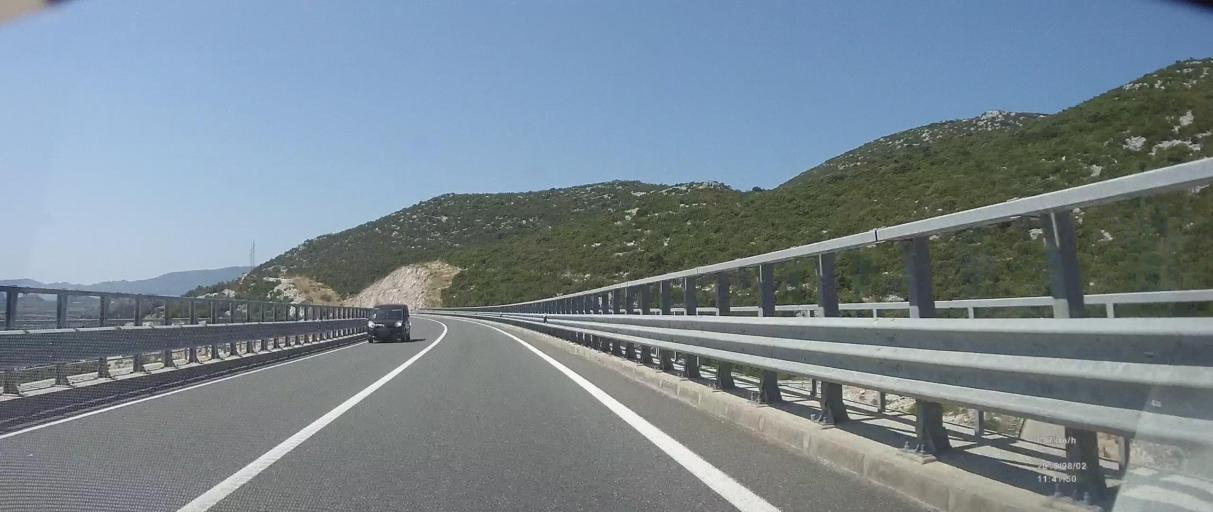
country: HR
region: Dubrovacko-Neretvanska
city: Komin
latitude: 43.0596
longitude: 17.4928
